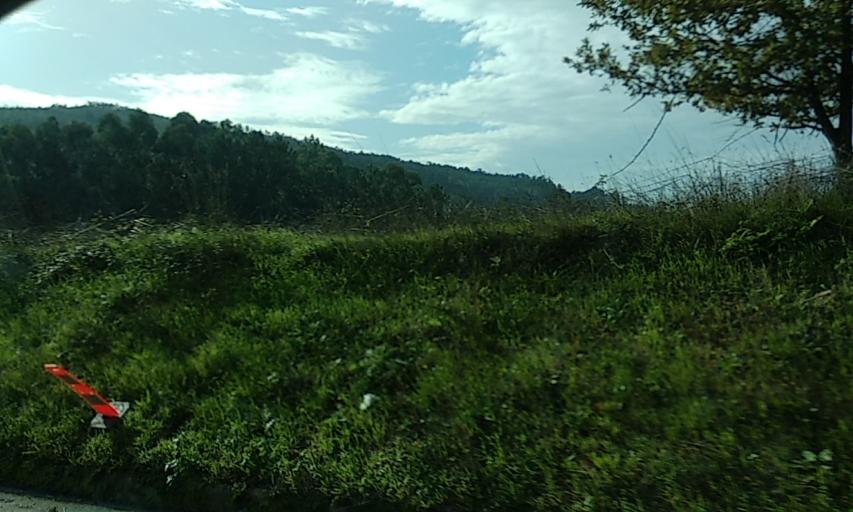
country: PT
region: Braga
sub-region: Braga
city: Oliveira
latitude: 41.4819
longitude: -8.4610
